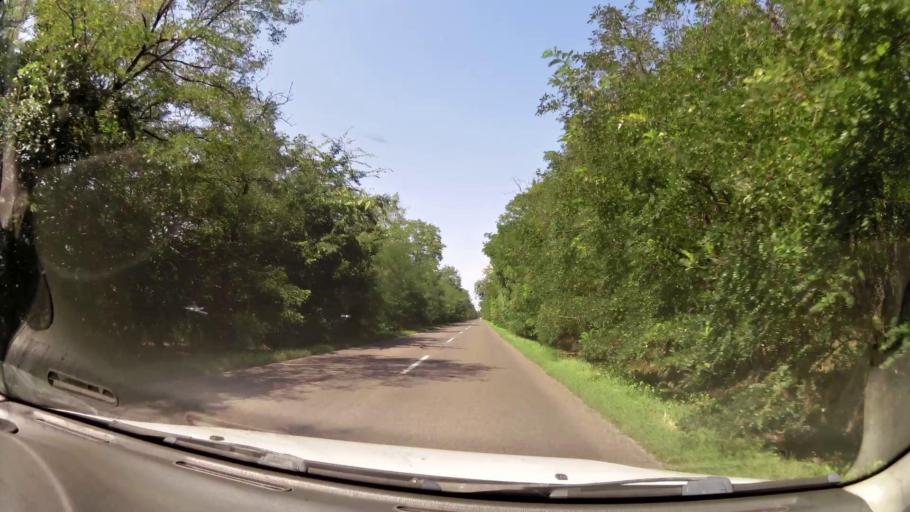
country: HU
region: Pest
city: Tapiosag
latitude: 47.3859
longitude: 19.6528
